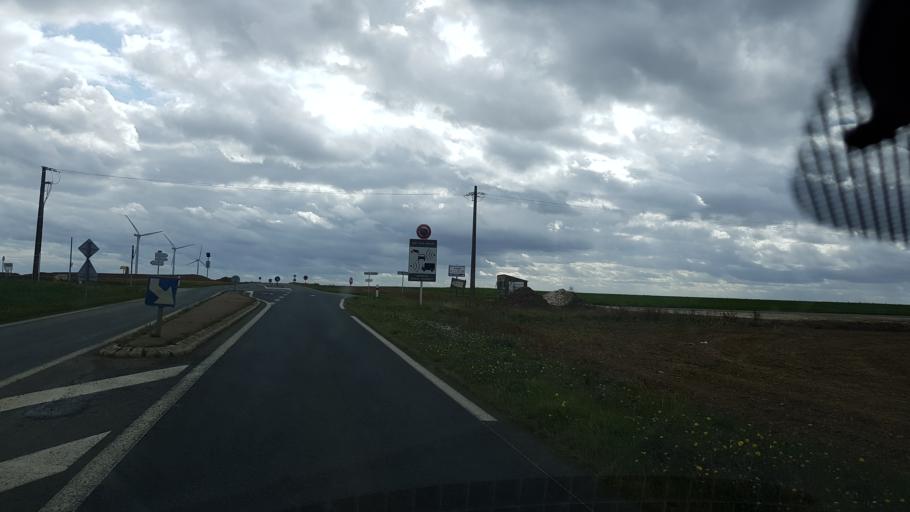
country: FR
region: Ile-de-France
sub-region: Departement de l'Essonne
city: Etampes
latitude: 48.4006
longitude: 2.1750
